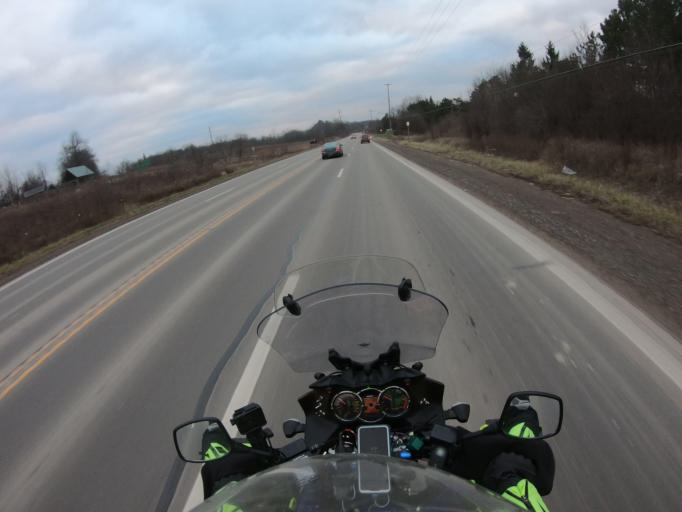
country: US
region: Michigan
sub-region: Oakland County
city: Holly
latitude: 42.8176
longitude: -83.5498
